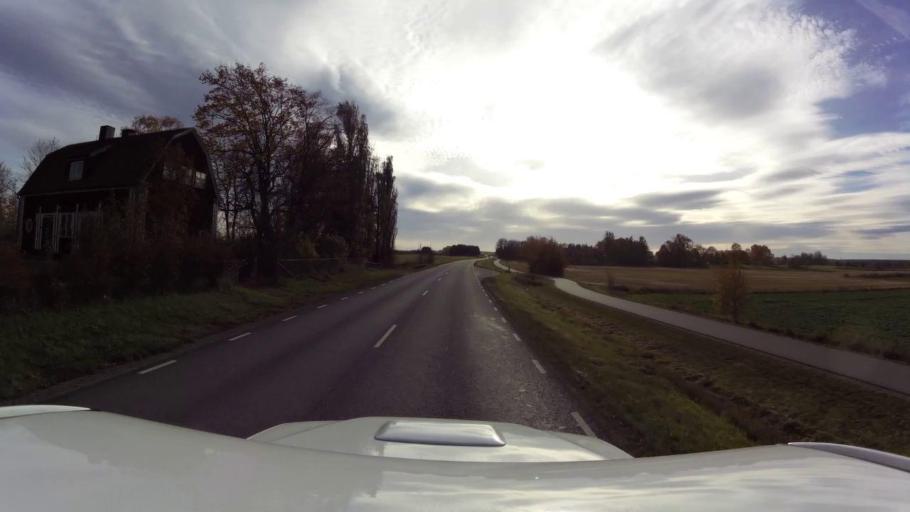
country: SE
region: OEstergoetland
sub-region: Linkopings Kommun
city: Ekangen
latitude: 58.4492
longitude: 15.6448
